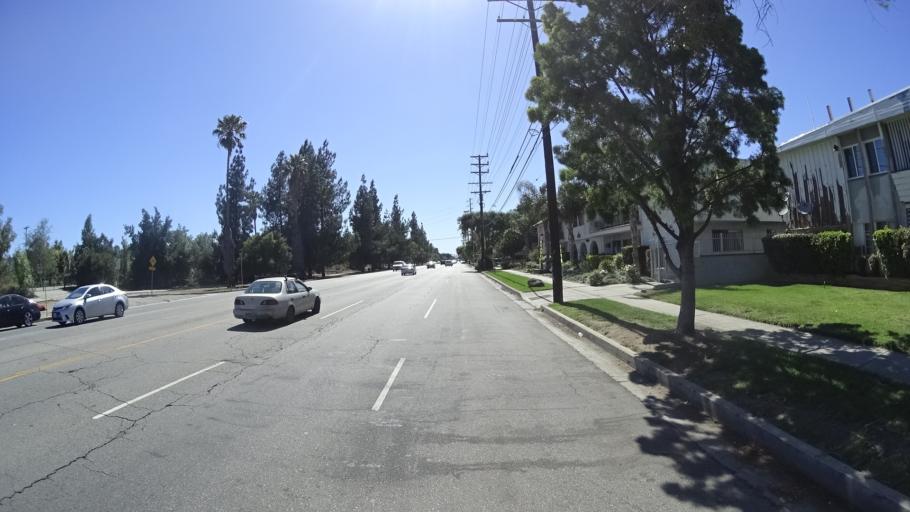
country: US
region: California
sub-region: Los Angeles County
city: Van Nuys
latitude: 34.1867
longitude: -118.4796
